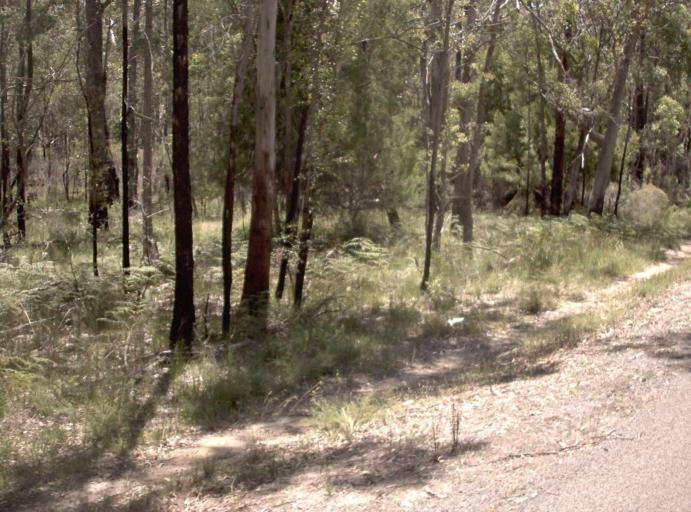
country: AU
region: Victoria
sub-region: East Gippsland
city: Lakes Entrance
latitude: -37.7704
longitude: 148.0581
